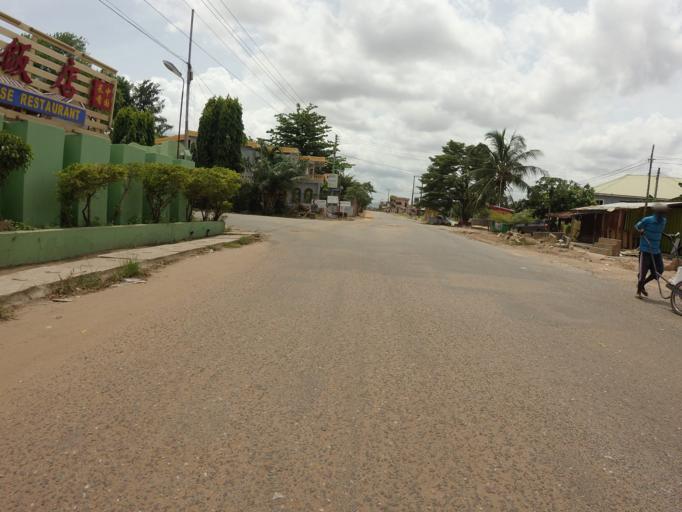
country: GH
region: Greater Accra
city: Dome
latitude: 5.6249
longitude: -0.2425
